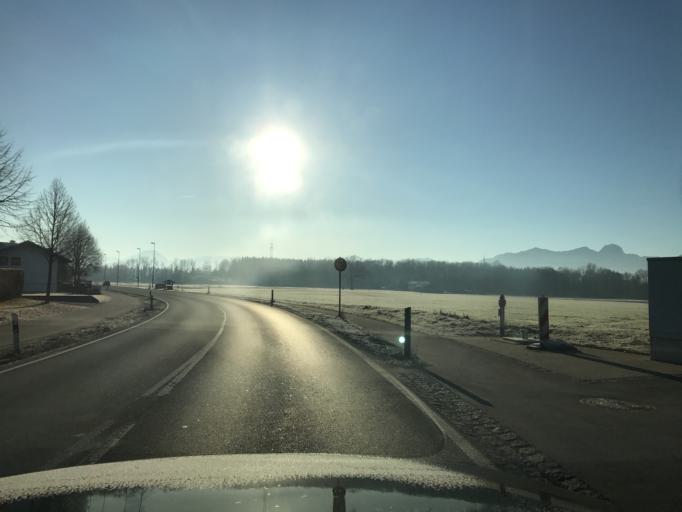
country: DE
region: Bavaria
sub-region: Upper Bavaria
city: Bad Aibling
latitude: 47.8475
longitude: 12.0195
